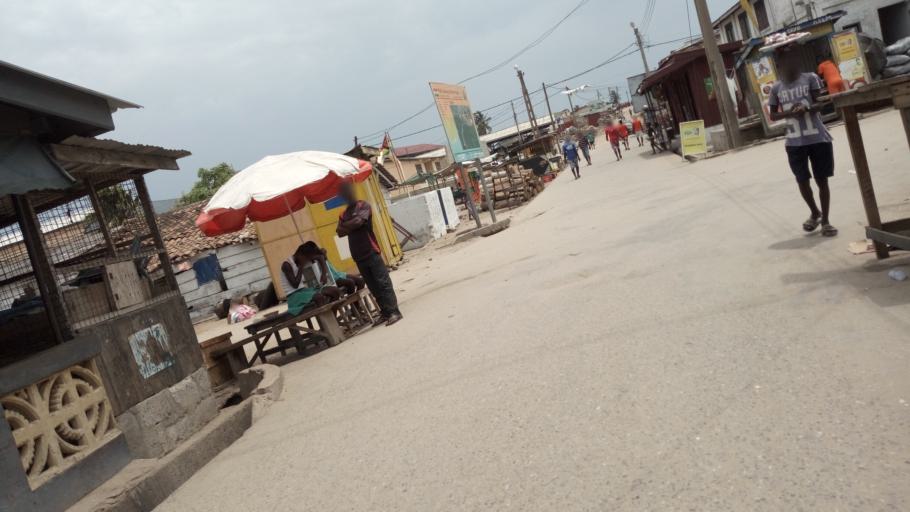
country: GH
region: Central
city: Winneba
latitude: 5.3386
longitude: -0.6188
